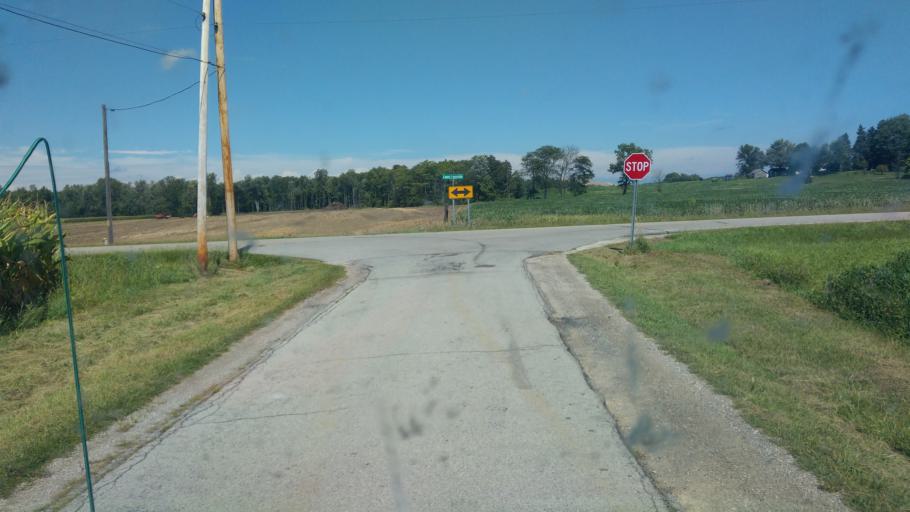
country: US
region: Ohio
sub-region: Crawford County
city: Bucyrus
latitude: 40.7983
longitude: -82.8731
